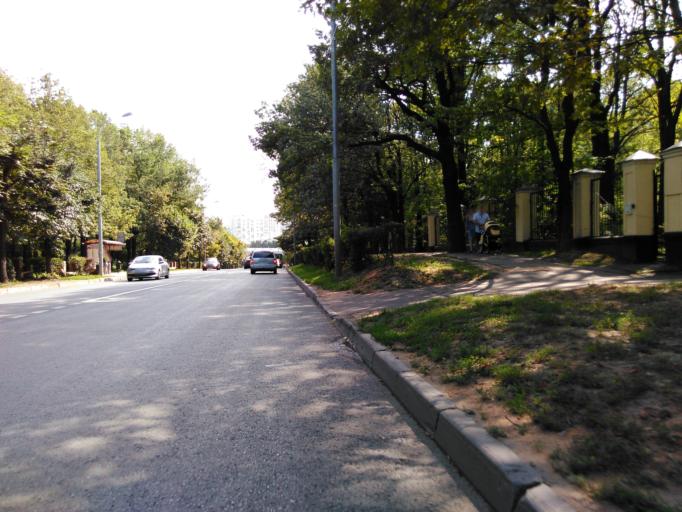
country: RU
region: Moskovskaya
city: Bol'shaya Setun'
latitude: 55.7181
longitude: 37.4015
